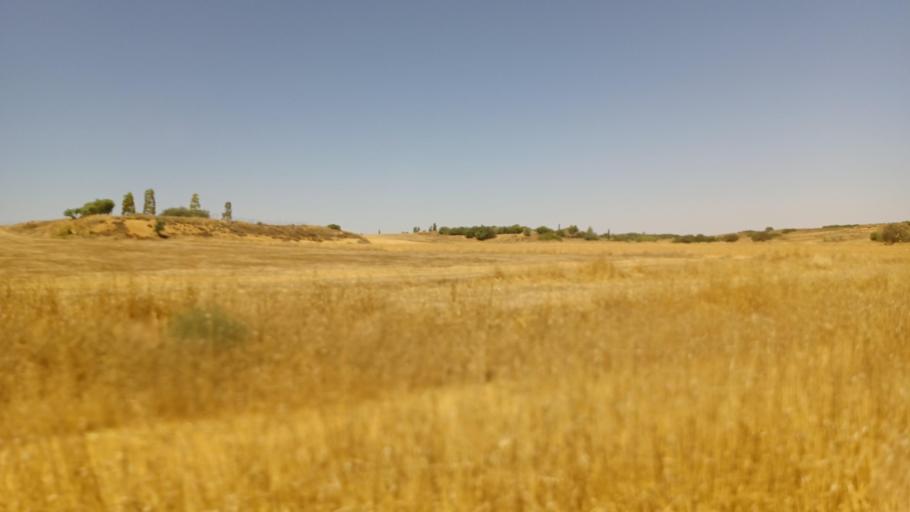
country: CY
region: Ammochostos
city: Avgorou
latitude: 35.0540
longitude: 33.8314
